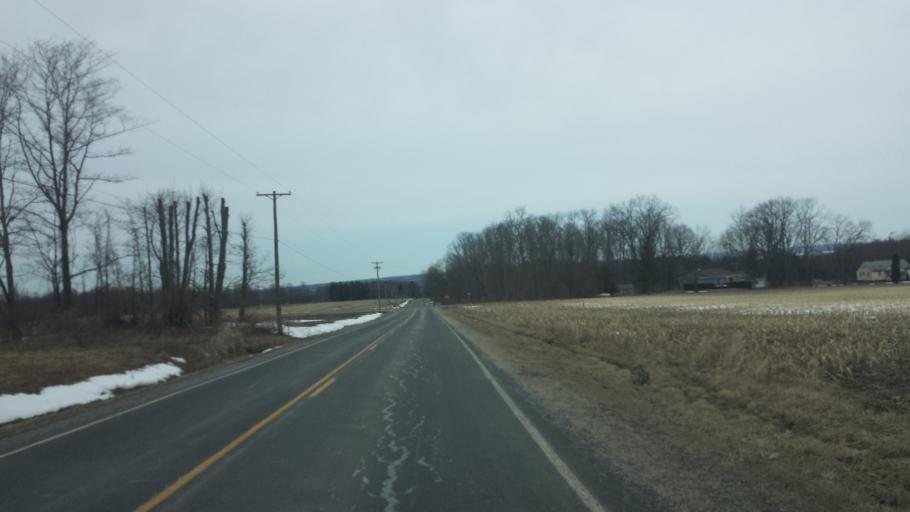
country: US
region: New York
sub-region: Tompkins County
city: Northwest Ithaca
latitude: 42.4948
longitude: -76.5740
